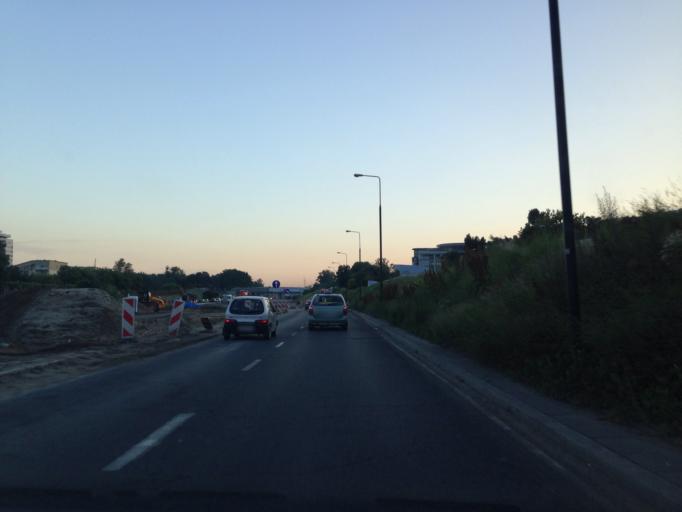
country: PL
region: Masovian Voivodeship
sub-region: Warszawa
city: Zoliborz
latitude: 52.2663
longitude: 20.9570
